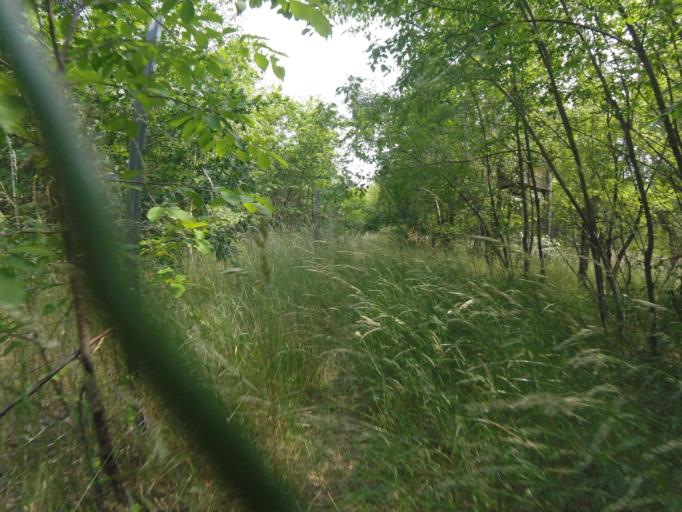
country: DE
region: Brandenburg
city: Konigs Wusterhausen
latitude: 52.3088
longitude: 13.6221
